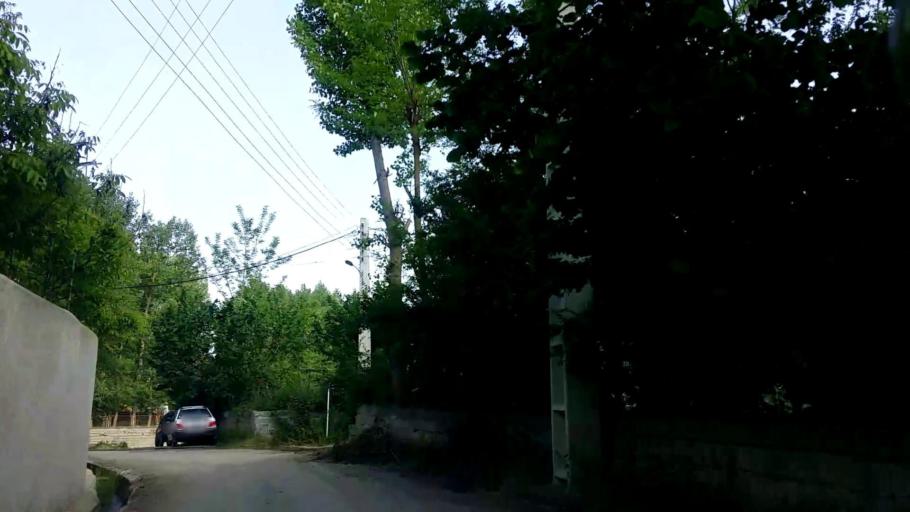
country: IR
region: Mazandaran
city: `Abbasabad
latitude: 36.5223
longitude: 51.1765
